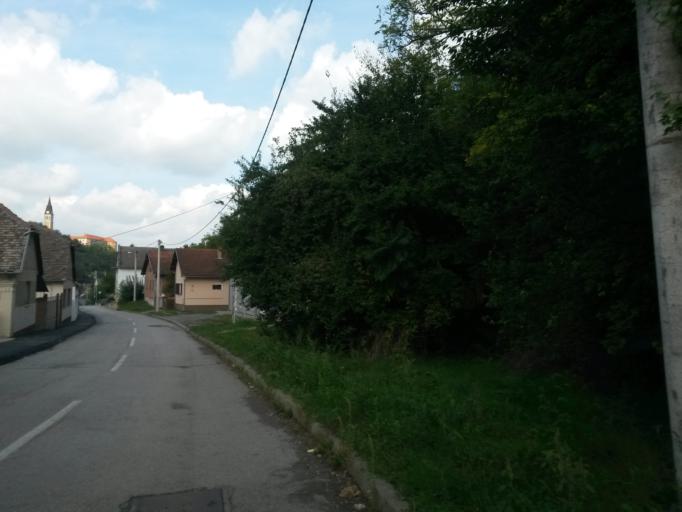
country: HR
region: Vukovarsko-Srijemska
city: Ilok
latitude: 45.2198
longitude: 19.3813
